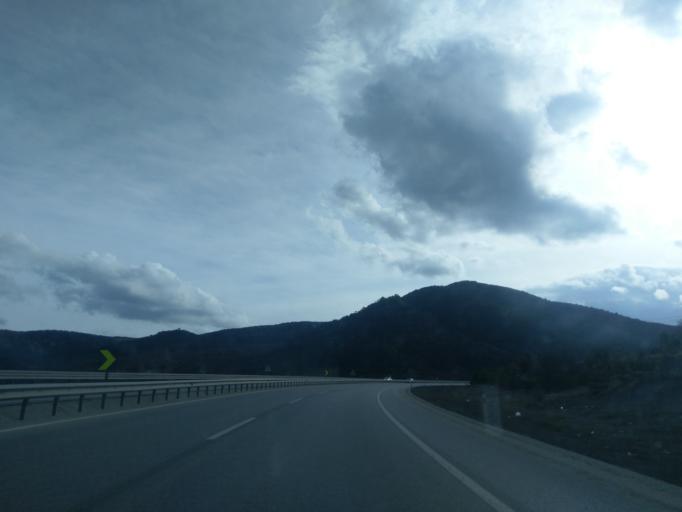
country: TR
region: Kuetahya
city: Sabuncu
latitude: 39.5605
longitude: 30.0765
